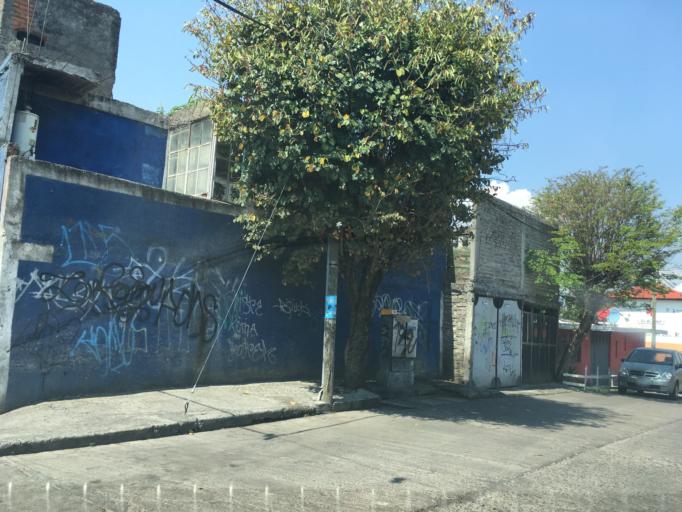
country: MX
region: Michoacan
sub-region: Morelia
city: Montana Monarca (Punta Altozano)
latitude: 19.6706
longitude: -101.1931
